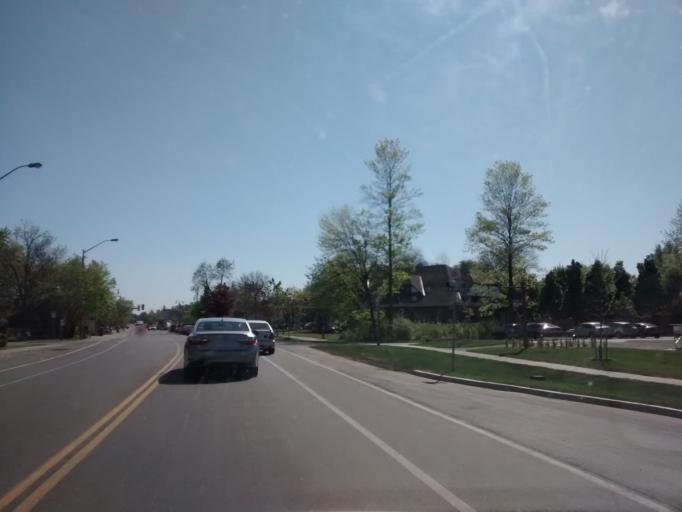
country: CA
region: Ontario
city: Oakville
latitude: 43.4001
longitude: -79.7055
